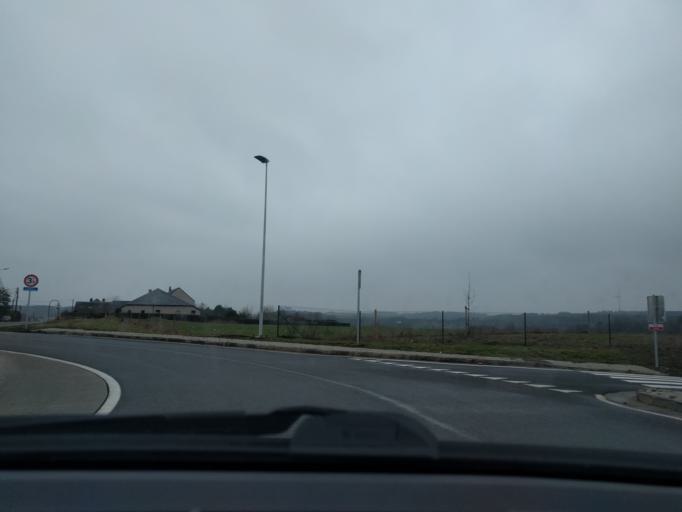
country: BE
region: Wallonia
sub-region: Province de Namur
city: Couvin
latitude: 50.0542
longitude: 4.5076
